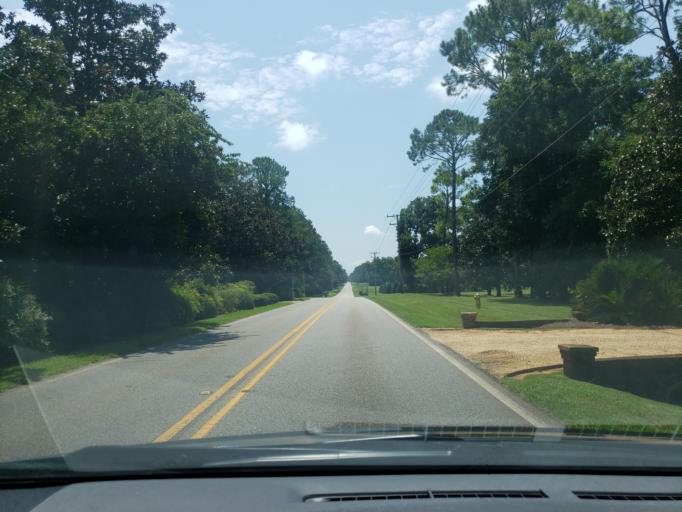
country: US
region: Georgia
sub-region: Dougherty County
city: Albany
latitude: 31.6084
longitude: -84.2756
